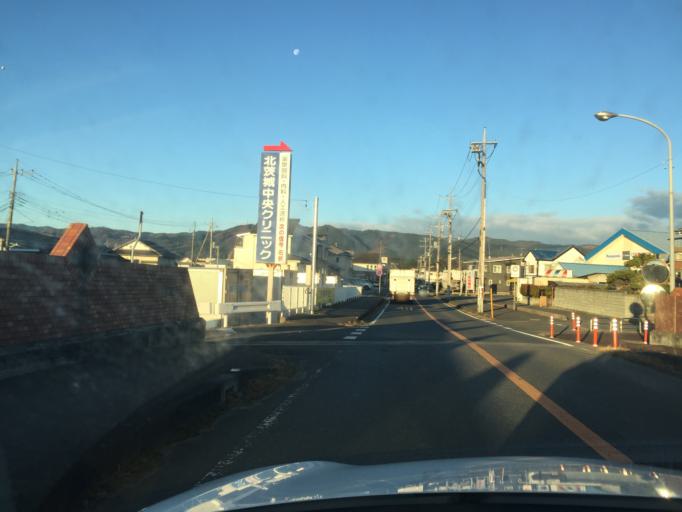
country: JP
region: Ibaraki
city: Kitaibaraki
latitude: 36.7912
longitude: 140.7376
